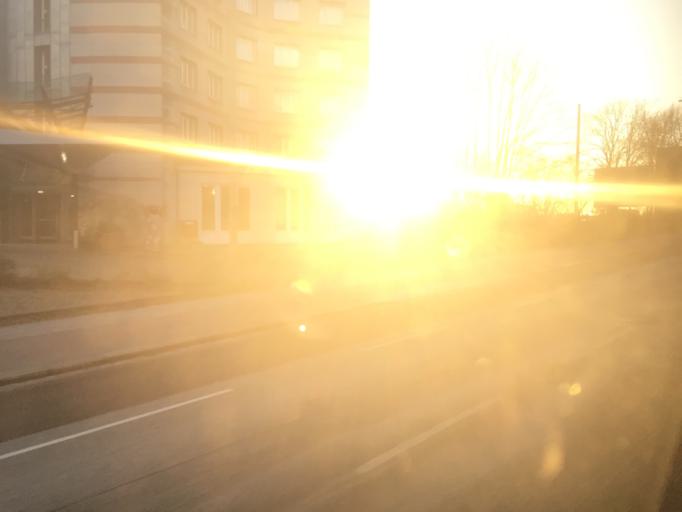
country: DE
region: Hamburg
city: Borgfelde
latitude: 53.5540
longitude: 10.0280
